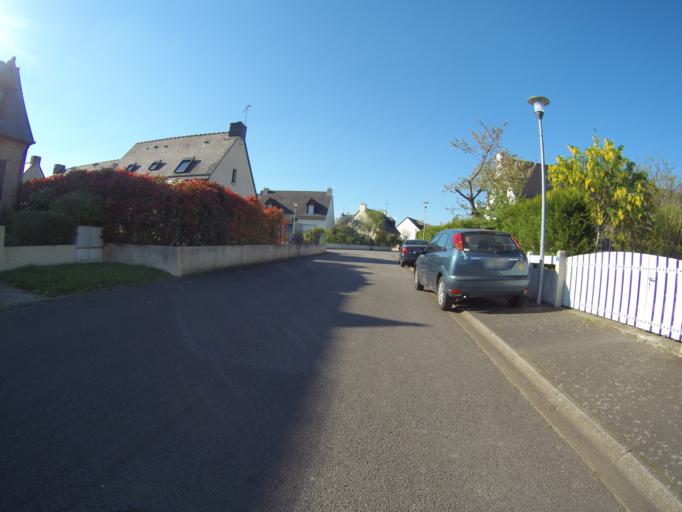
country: FR
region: Brittany
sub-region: Departement d'Ille-et-Vilaine
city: Vern-sur-Seiche
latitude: 48.0386
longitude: -1.5992
